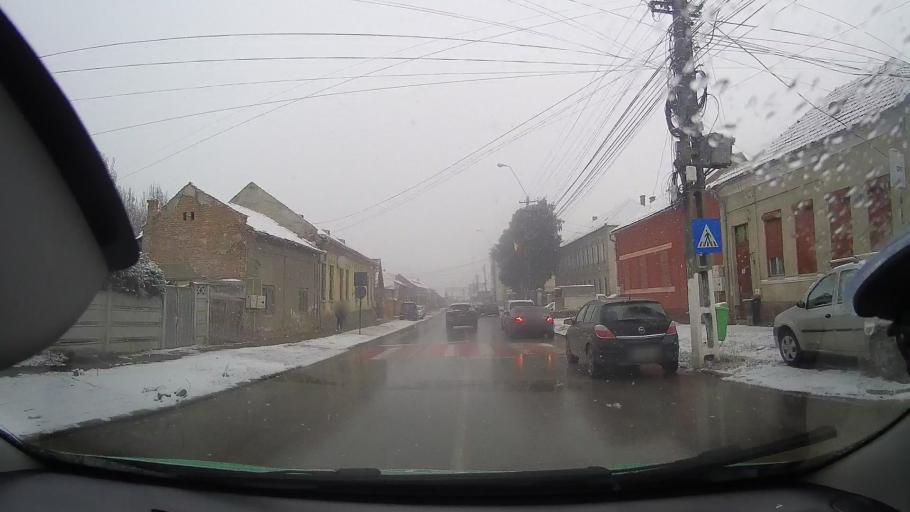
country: RO
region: Alba
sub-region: Municipiul Aiud
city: Aiud
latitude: 46.3086
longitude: 23.7233
